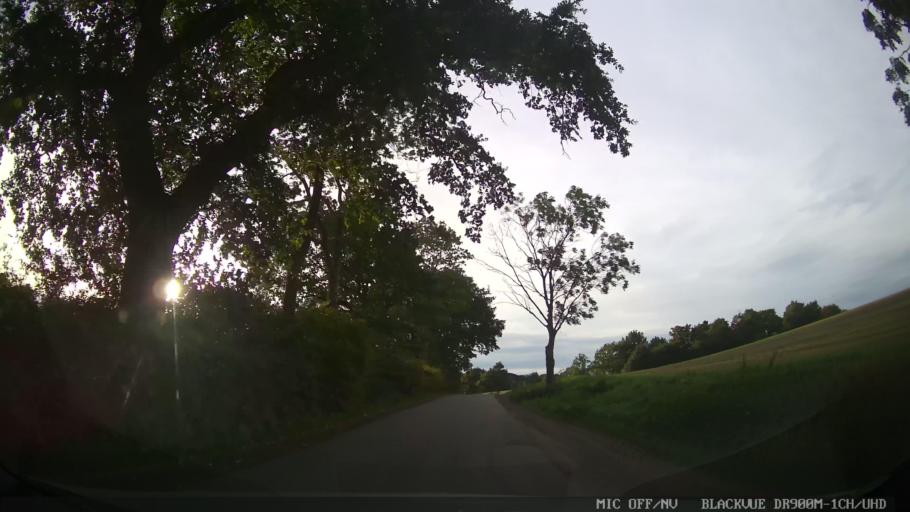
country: DE
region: Schleswig-Holstein
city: Grube
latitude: 54.2655
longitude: 11.0522
